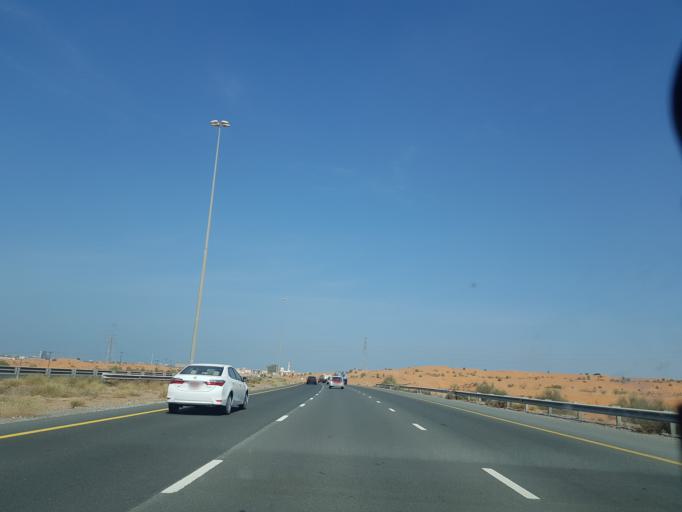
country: AE
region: Ra's al Khaymah
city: Ras al-Khaimah
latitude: 25.6795
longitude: 55.8837
